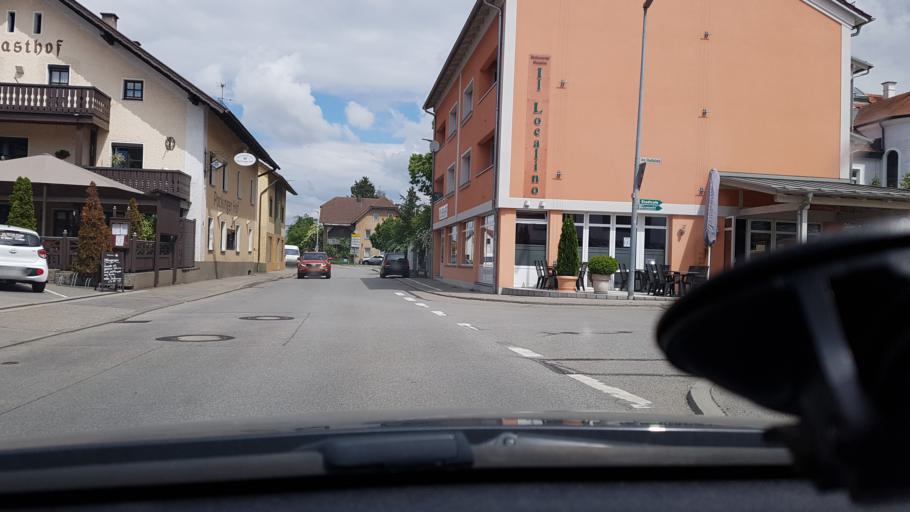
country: DE
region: Bavaria
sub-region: Lower Bavaria
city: Pocking
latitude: 48.4027
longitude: 13.3108
